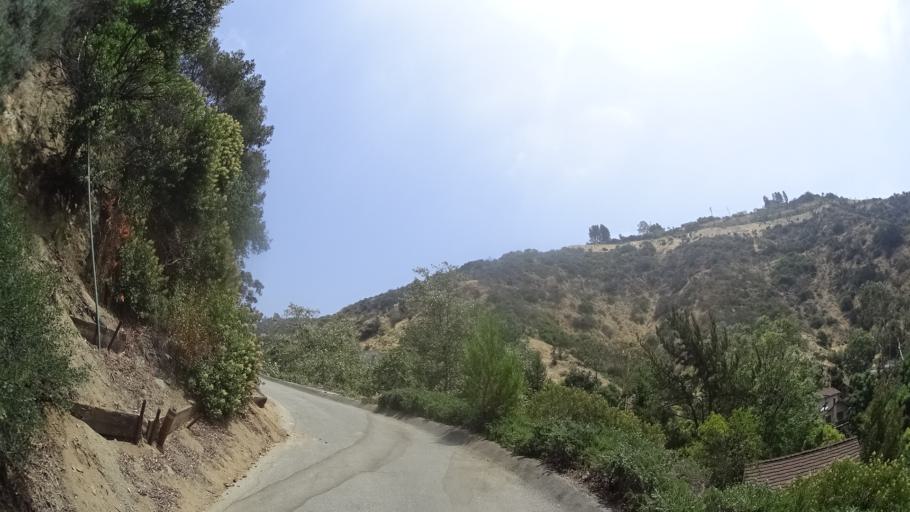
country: US
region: California
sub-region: Los Angeles County
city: West Hollywood
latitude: 34.1115
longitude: -118.3615
